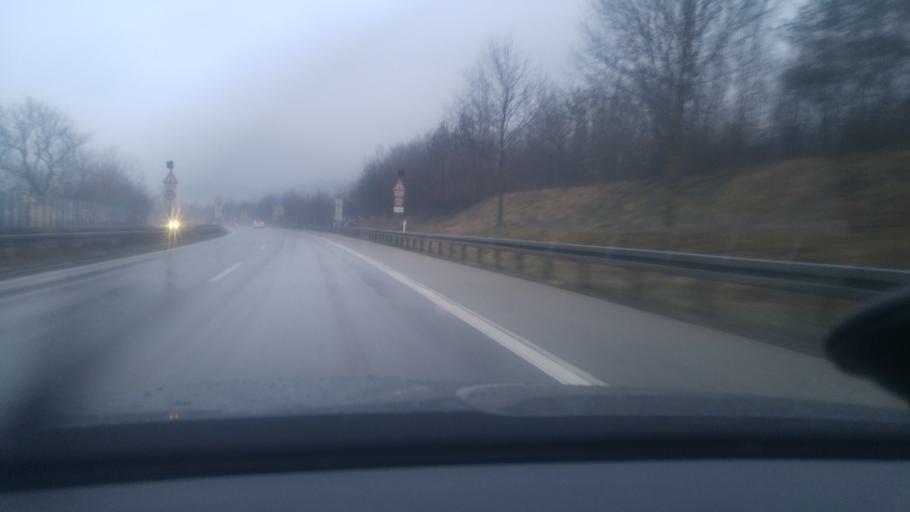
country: DE
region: Baden-Wuerttemberg
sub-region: Freiburg Region
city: Kirchzarten
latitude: 47.9779
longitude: 7.9160
